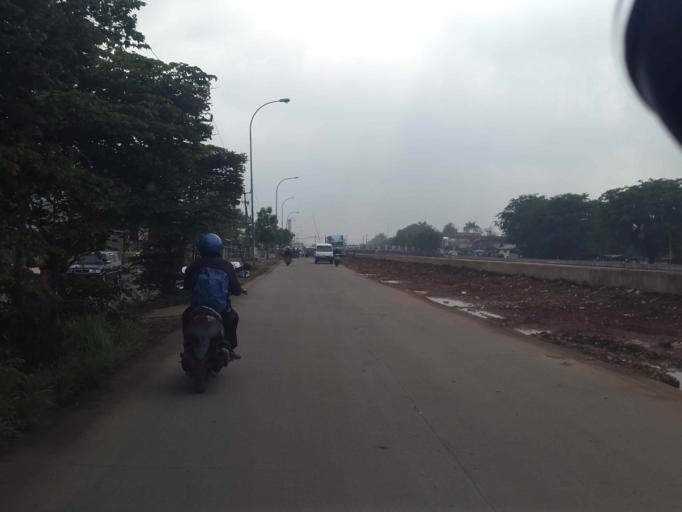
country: ID
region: West Java
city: Cikarang
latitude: -6.2813
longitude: 107.0906
